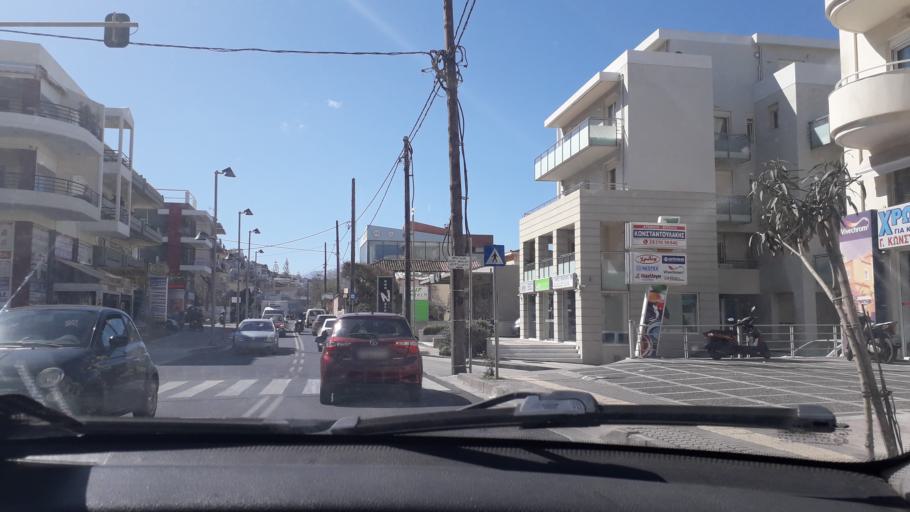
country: GR
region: Crete
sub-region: Nomos Rethymnis
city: Rethymno
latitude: 35.3658
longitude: 24.4660
